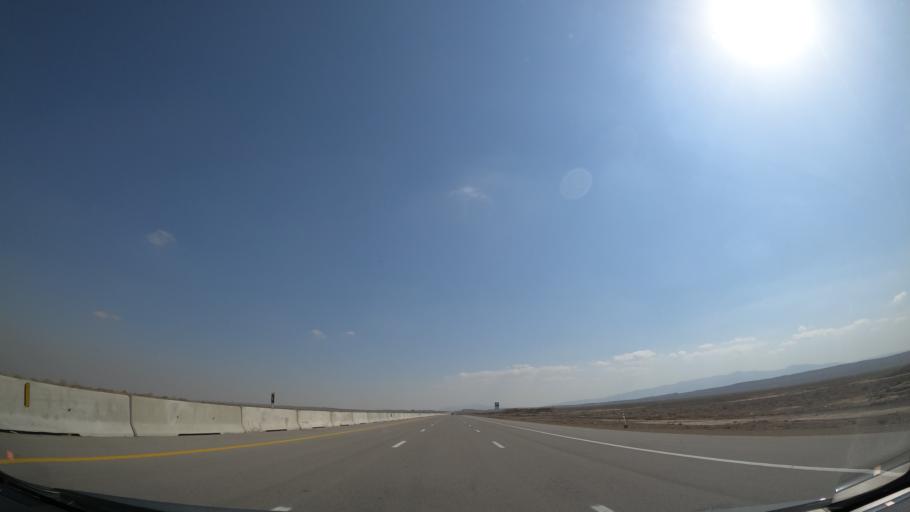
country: IR
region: Alborz
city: Nazarabad
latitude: 35.8215
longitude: 50.5129
